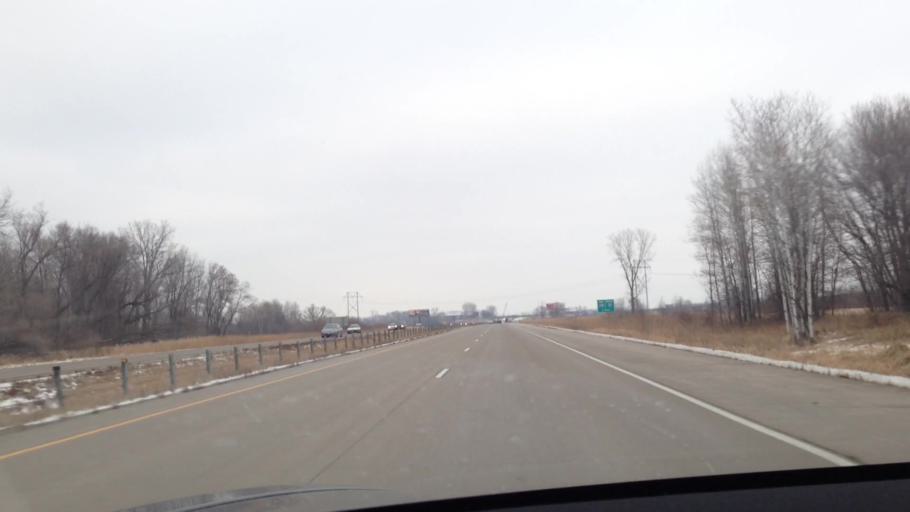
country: US
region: Minnesota
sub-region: Anoka County
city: Centerville
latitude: 45.2073
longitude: -93.0435
